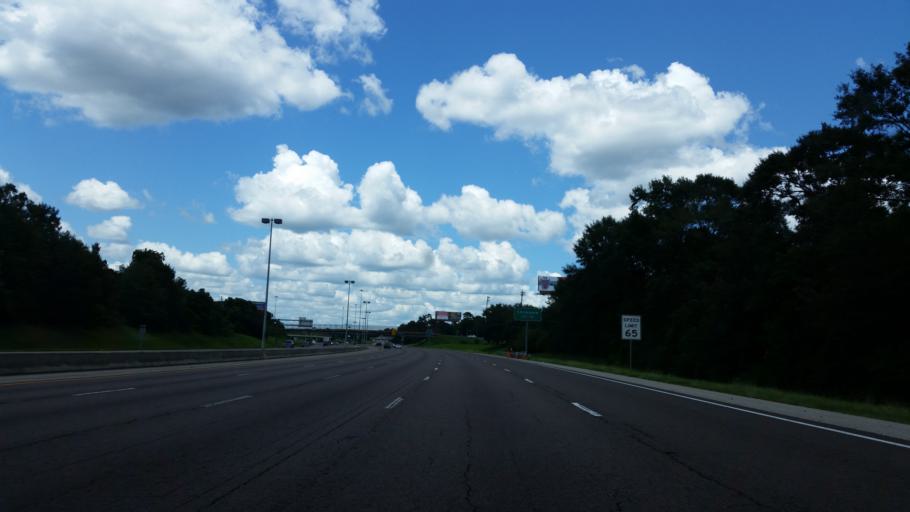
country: US
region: Alabama
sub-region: Mobile County
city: Chickasaw
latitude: 30.7598
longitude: -88.0923
